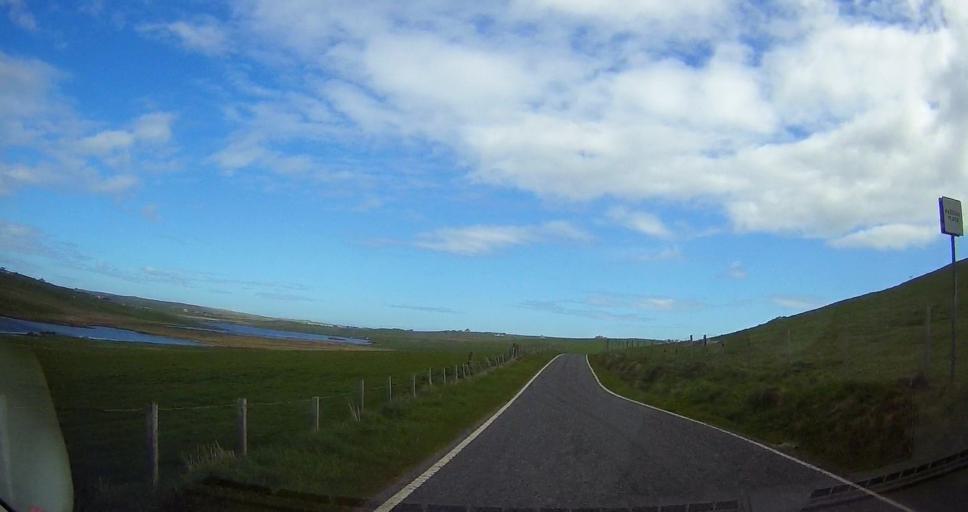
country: GB
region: Scotland
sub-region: Shetland Islands
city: Sandwick
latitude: 59.9243
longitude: -1.3350
